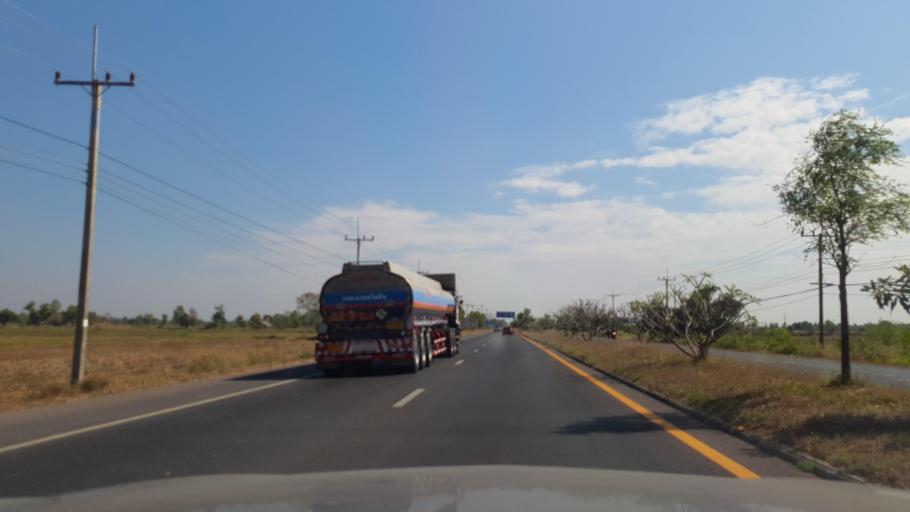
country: TH
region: Maha Sarakham
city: Chiang Yuen
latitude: 16.3760
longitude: 103.1682
